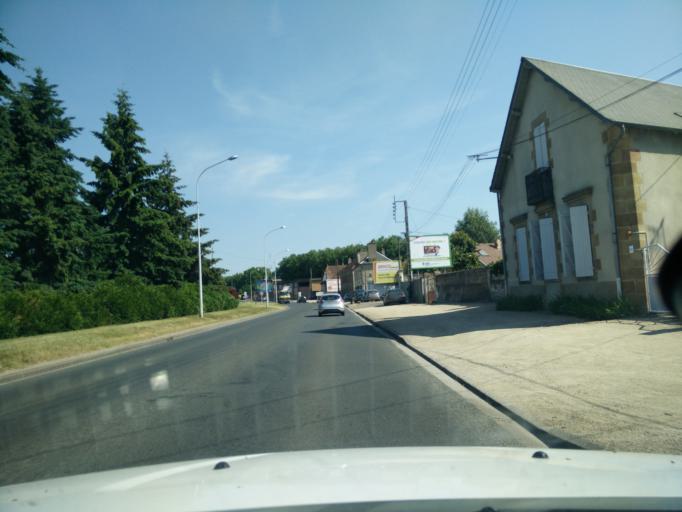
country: FR
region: Auvergne
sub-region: Departement de l'Allier
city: Moulins
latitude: 46.5584
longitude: 3.3214
